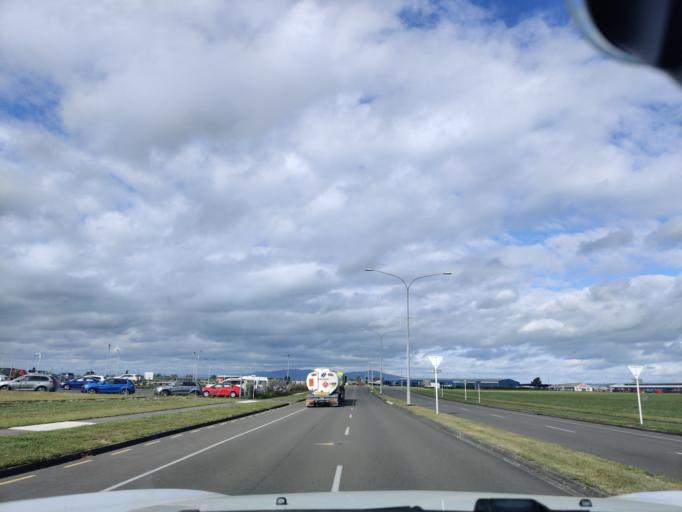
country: NZ
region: Manawatu-Wanganui
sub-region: Palmerston North City
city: Palmerston North
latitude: -40.3257
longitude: 175.6218
